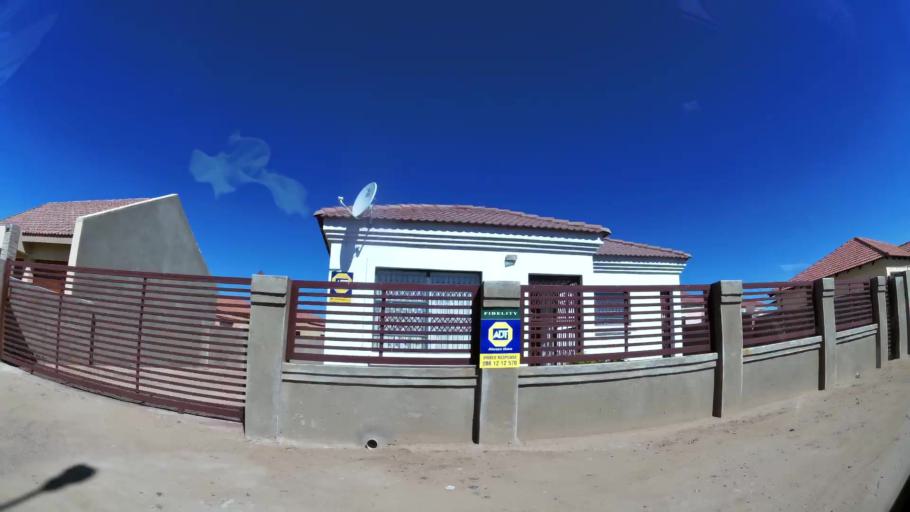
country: ZA
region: Limpopo
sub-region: Capricorn District Municipality
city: Polokwane
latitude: -23.8706
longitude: 29.4209
